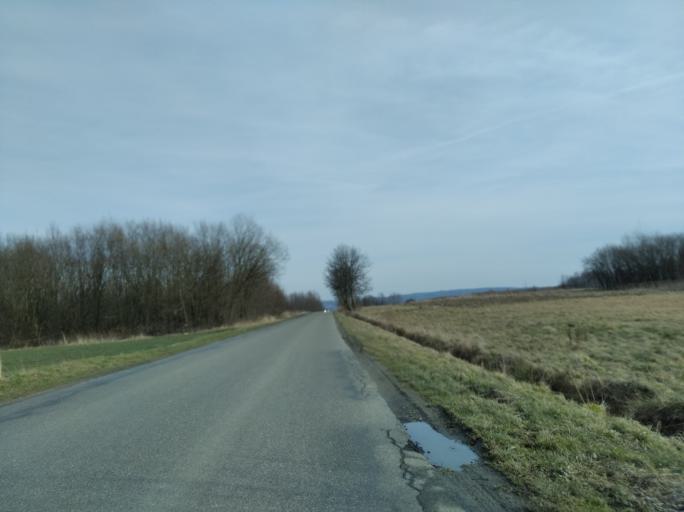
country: PL
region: Subcarpathian Voivodeship
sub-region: Powiat brzozowski
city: Stara Wies
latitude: 49.7132
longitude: 21.9898
